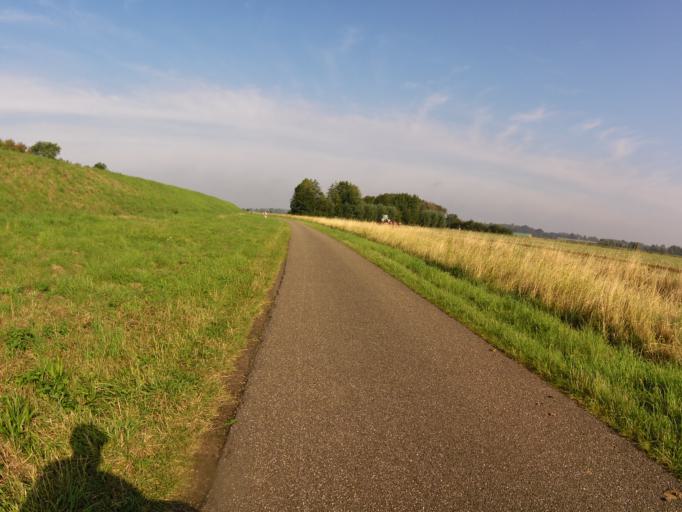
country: DE
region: Lower Saxony
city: Langwedel
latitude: 52.9610
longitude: 9.1757
